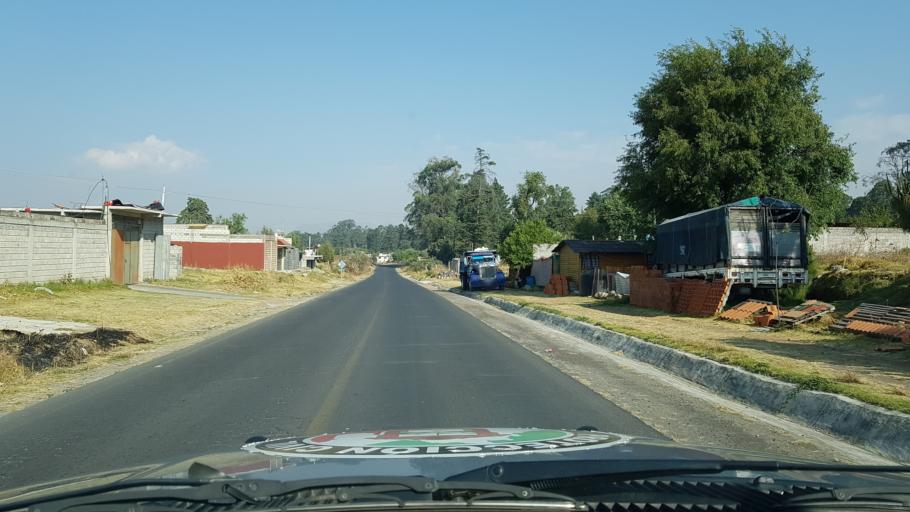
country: MX
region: Mexico
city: Ozumba de Alzate
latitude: 19.0506
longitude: -98.7819
